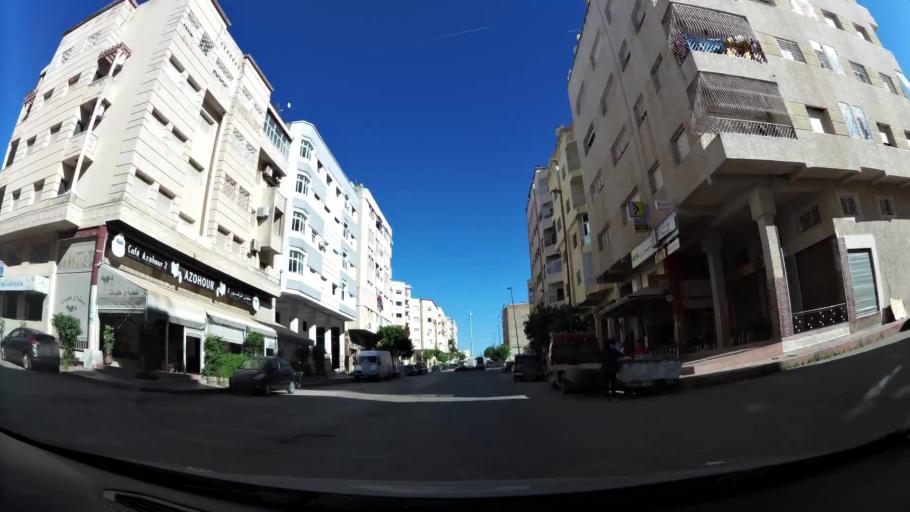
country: MA
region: Fes-Boulemane
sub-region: Fes
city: Fes
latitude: 34.0101
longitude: -4.9657
